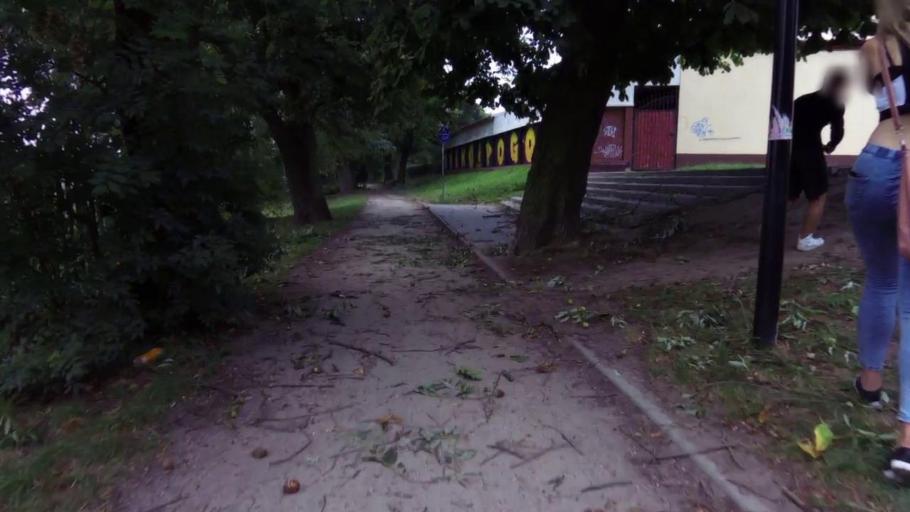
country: PL
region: West Pomeranian Voivodeship
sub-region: Powiat choszczenski
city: Choszczno
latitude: 53.1618
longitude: 15.4235
